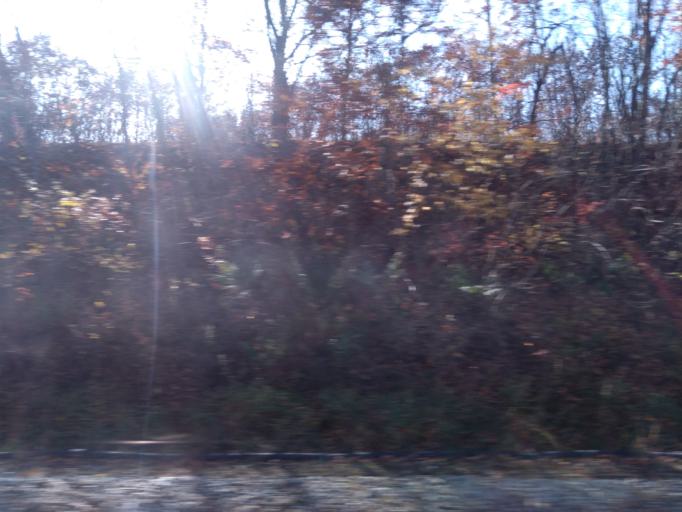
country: JP
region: Hokkaido
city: Chitose
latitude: 42.7830
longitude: 141.7049
